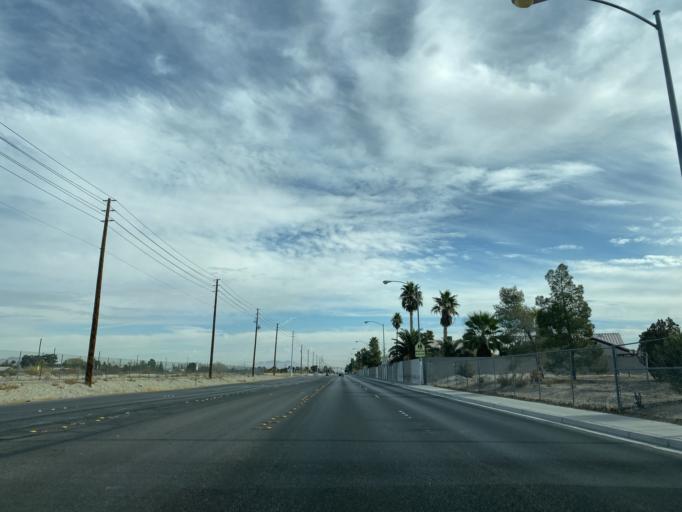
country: US
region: Nevada
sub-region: Clark County
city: North Las Vegas
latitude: 36.2467
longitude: -115.1961
